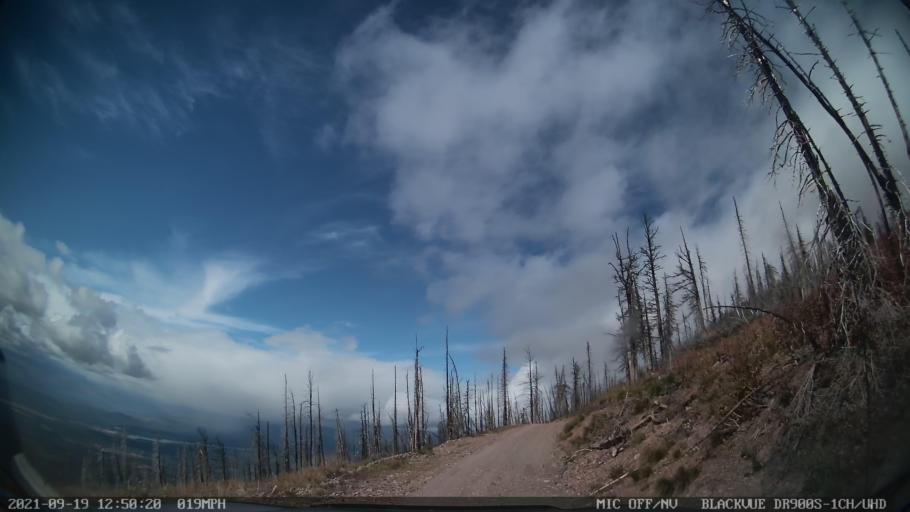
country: US
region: Montana
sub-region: Missoula County
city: Seeley Lake
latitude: 47.1851
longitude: -113.3566
